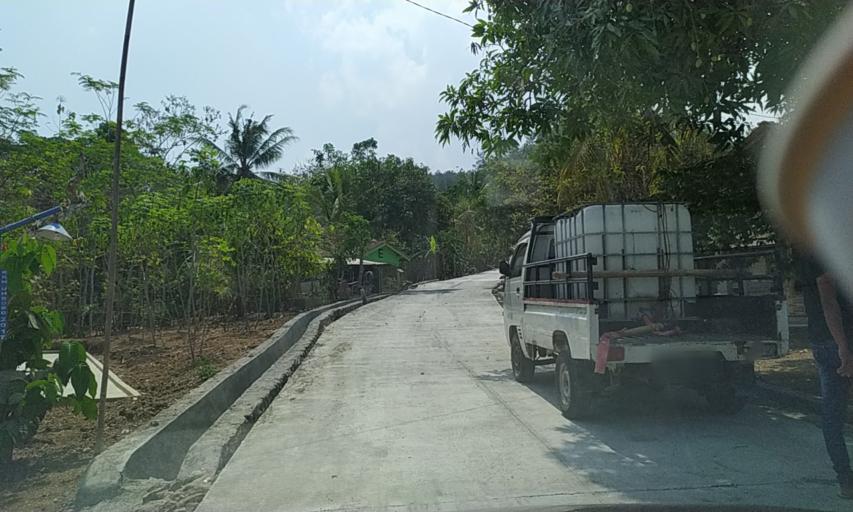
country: ID
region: Central Java
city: Ciloning
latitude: -7.4770
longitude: 108.8450
